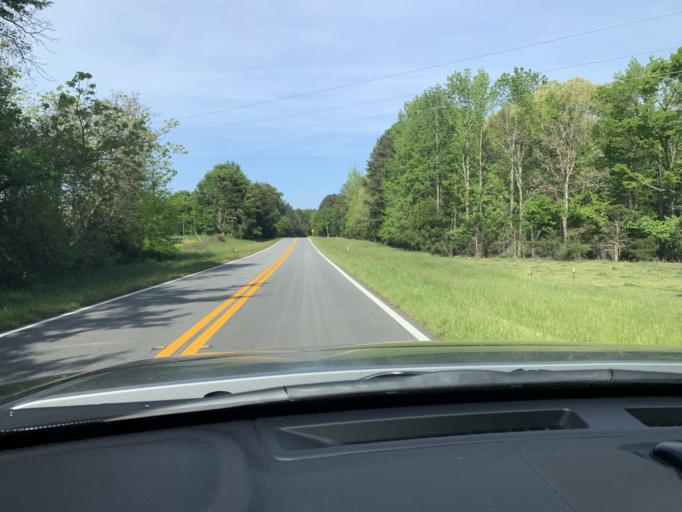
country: US
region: Georgia
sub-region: Oconee County
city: Watkinsville
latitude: 33.8131
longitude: -83.4161
